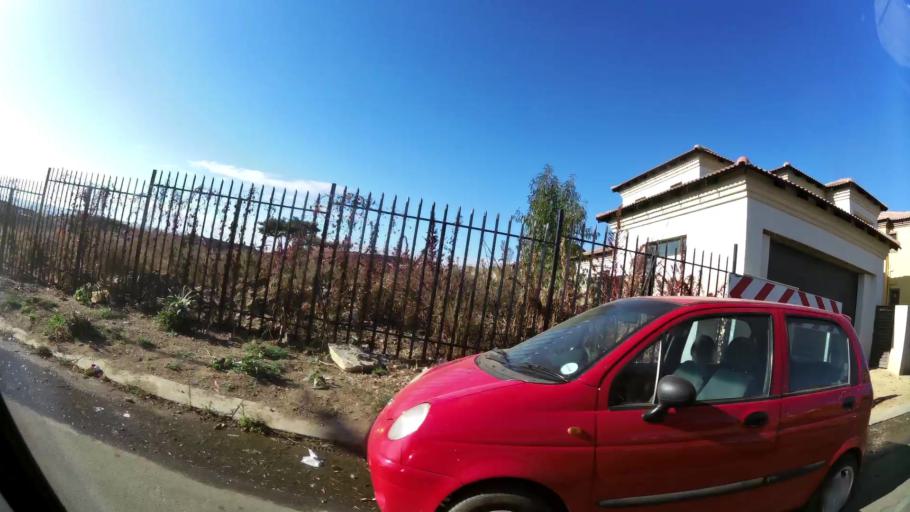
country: ZA
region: Gauteng
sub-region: City of Tshwane Metropolitan Municipality
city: Centurion
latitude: -25.8963
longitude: 28.0995
